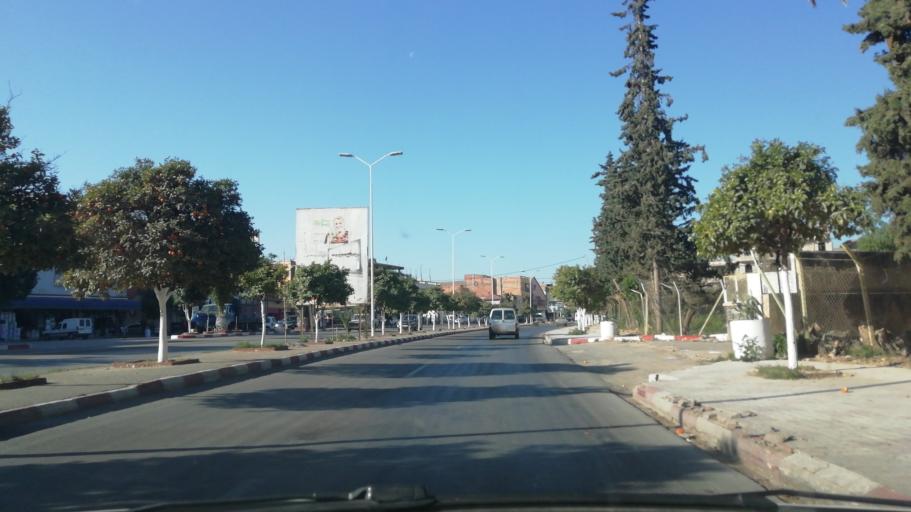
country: DZ
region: Mascara
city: Mascara
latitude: 35.5962
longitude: 0.0779
